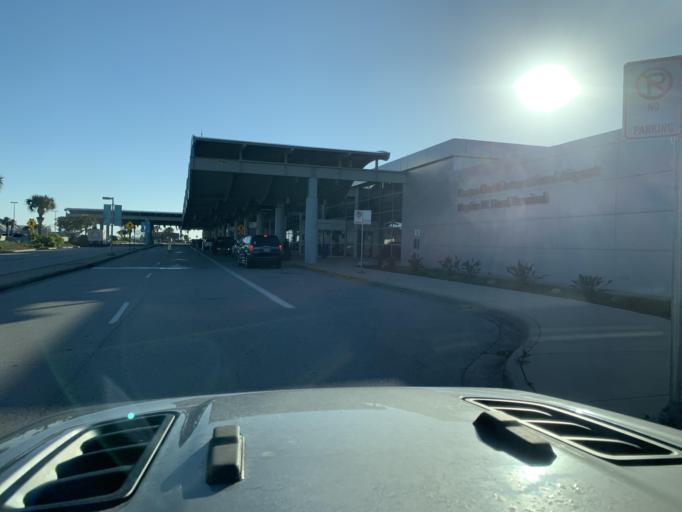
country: US
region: Texas
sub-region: Nueces County
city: Corpus Christi
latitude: 27.7747
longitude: -97.5036
